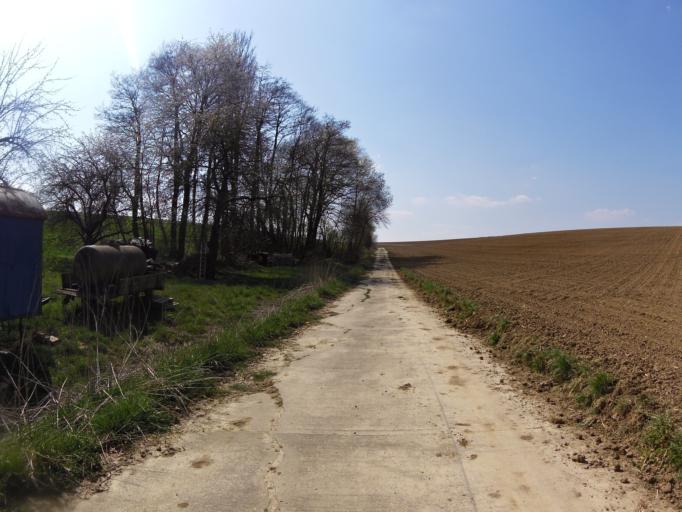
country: DE
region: Bavaria
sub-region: Regierungsbezirk Unterfranken
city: Dettelbach
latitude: 49.8189
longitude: 10.1445
